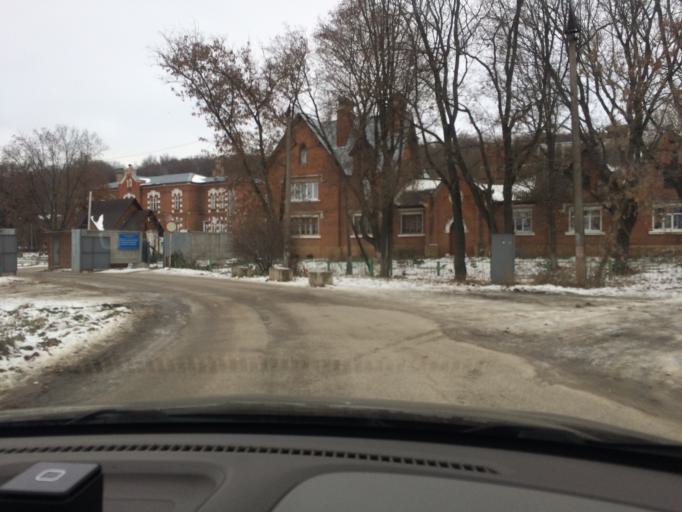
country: RU
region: Tula
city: Plavsk
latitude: 53.7183
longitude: 37.2924
